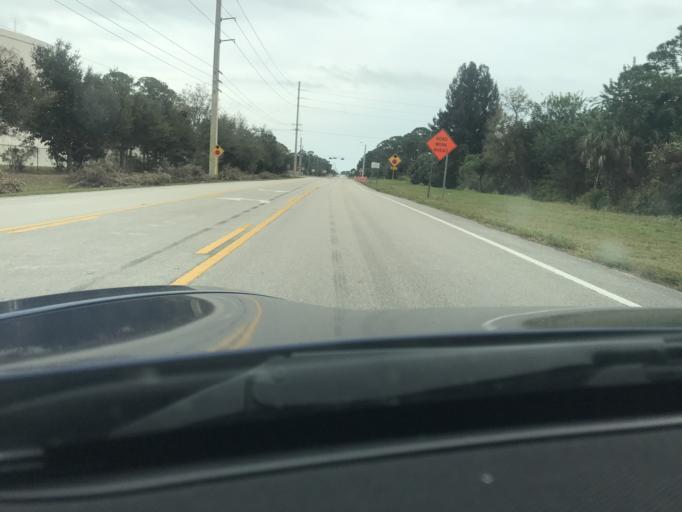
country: US
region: Florida
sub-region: Indian River County
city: Winter Beach
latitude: 27.7339
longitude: -80.4475
